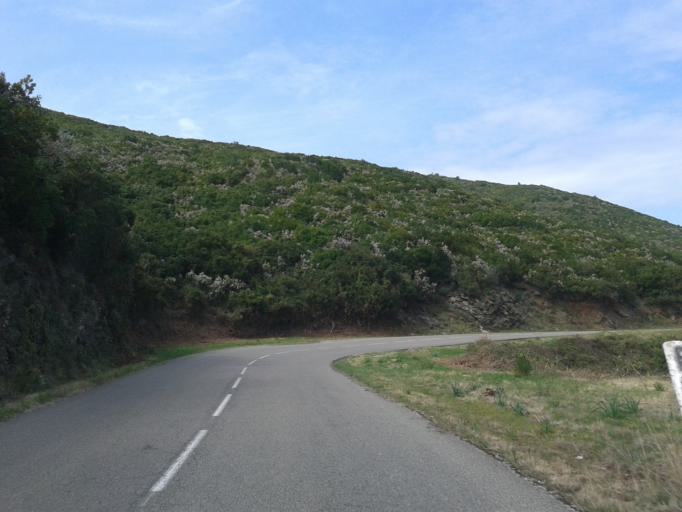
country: FR
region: Corsica
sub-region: Departement de la Haute-Corse
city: Brando
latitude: 42.8531
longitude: 9.4837
